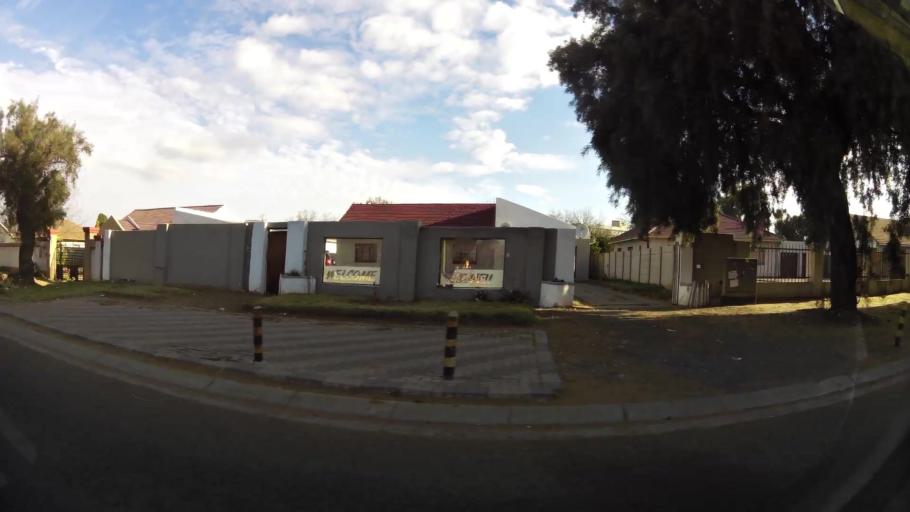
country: ZA
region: Orange Free State
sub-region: Lejweleputswa District Municipality
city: Welkom
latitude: -27.9915
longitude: 26.7475
